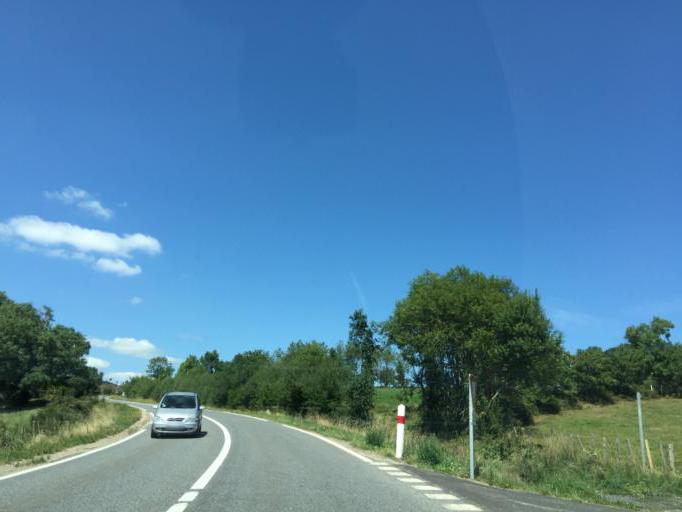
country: FR
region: Midi-Pyrenees
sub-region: Departement de l'Aveyron
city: Laguiole
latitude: 44.6498
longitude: 2.8521
